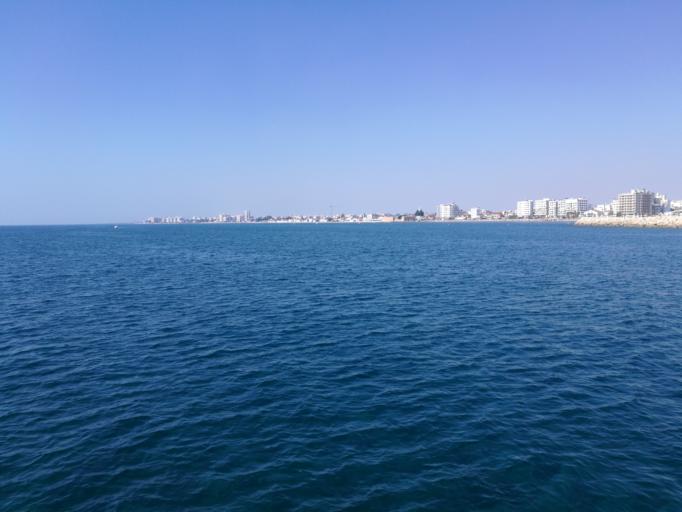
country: CY
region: Larnaka
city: Larnaca
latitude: 34.9177
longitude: 33.6445
